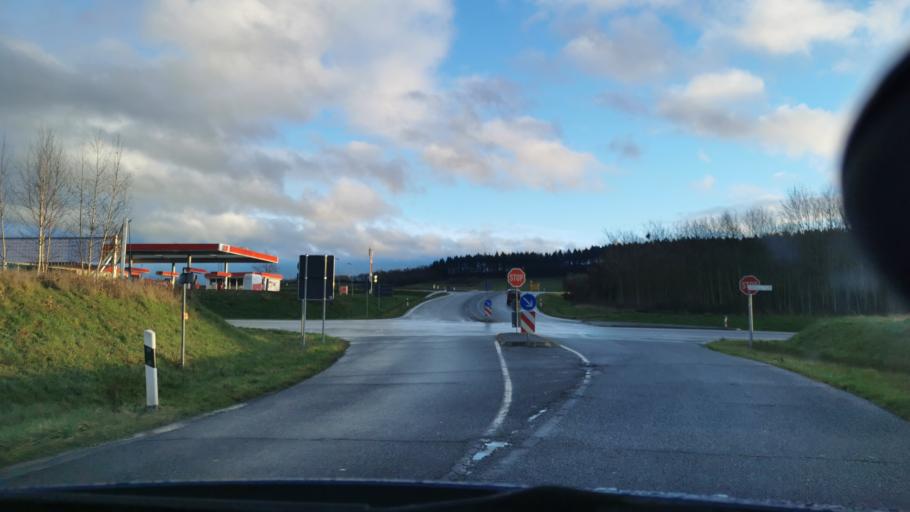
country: DE
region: Rheinland-Pfalz
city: Brauneberg
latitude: 49.9241
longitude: 6.9843
